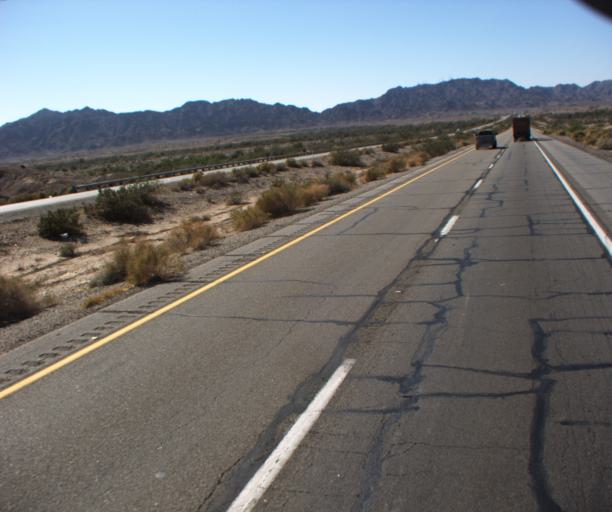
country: US
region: Arizona
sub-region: Yuma County
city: Wellton
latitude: 32.6621
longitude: -114.2627
